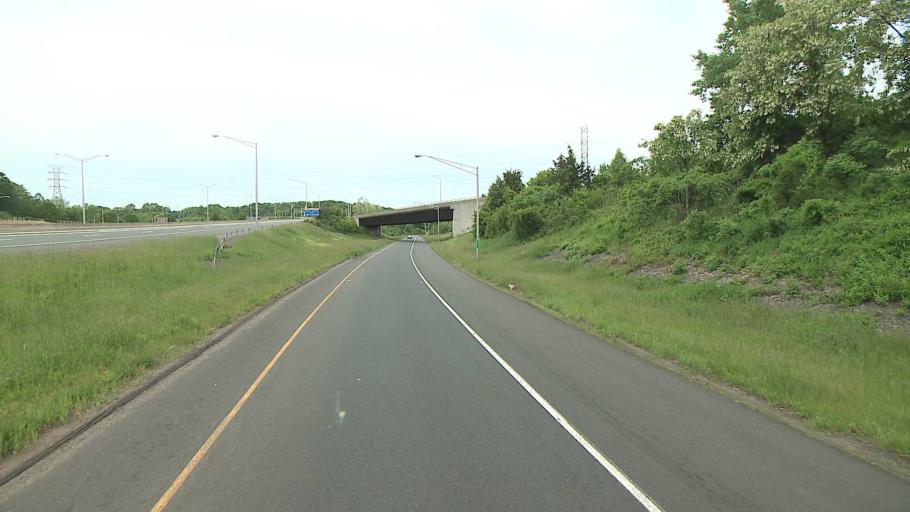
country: US
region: Connecticut
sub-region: Hartford County
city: East Hartford
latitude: 41.7678
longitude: -72.5761
